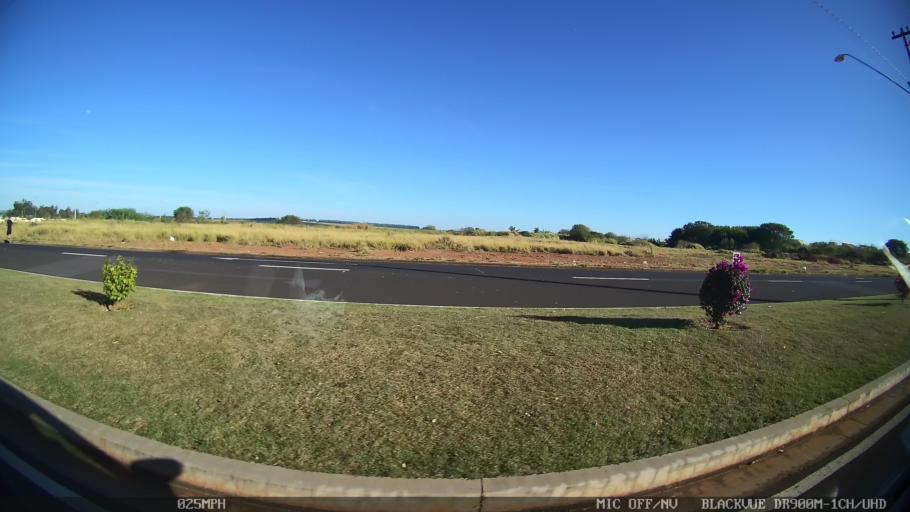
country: BR
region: Sao Paulo
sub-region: Franca
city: Franca
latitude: -20.5754
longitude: -47.4093
